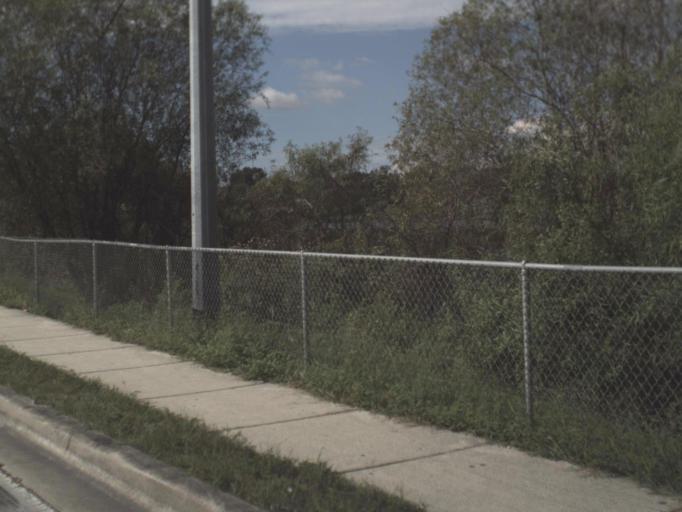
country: US
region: Florida
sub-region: Polk County
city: Crystal Lake
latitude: 28.0275
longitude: -81.9074
